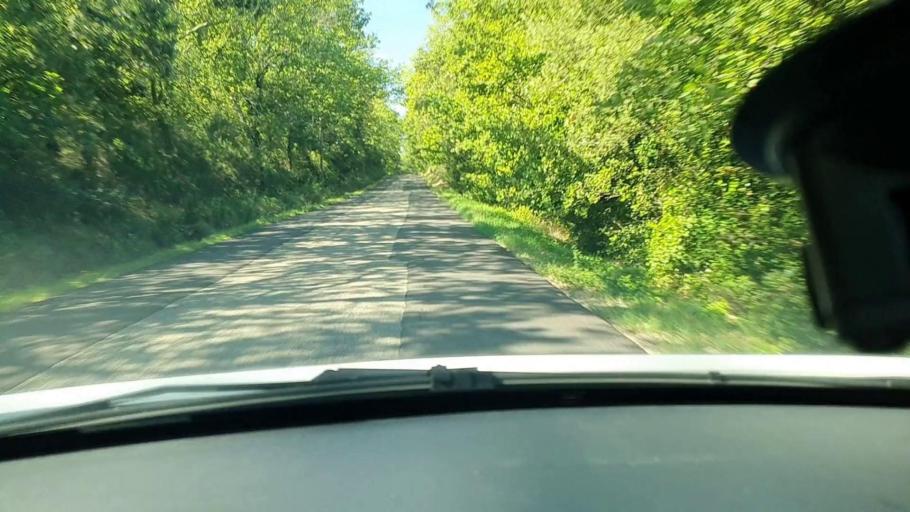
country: FR
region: Languedoc-Roussillon
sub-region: Departement du Gard
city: Sabran
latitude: 44.1748
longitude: 4.5101
